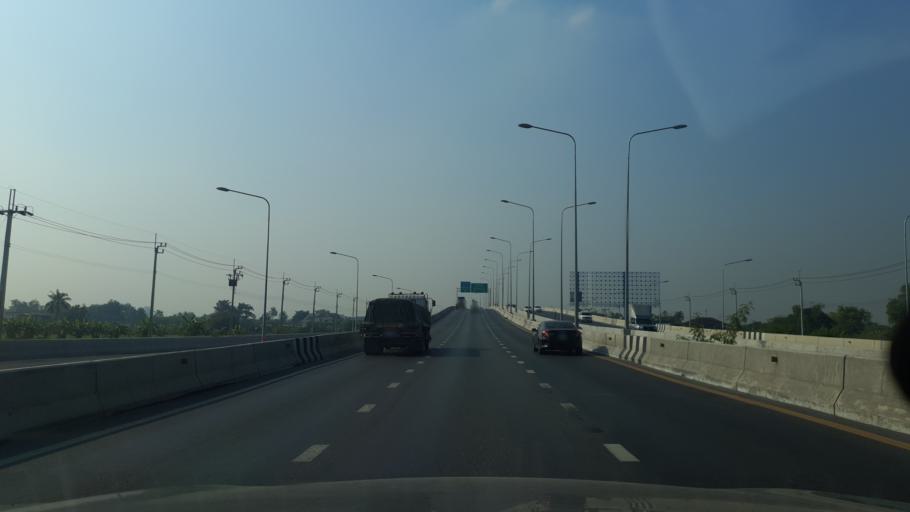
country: TH
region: Nonthaburi
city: Bang Bua Thong
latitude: 13.9642
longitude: 100.4608
